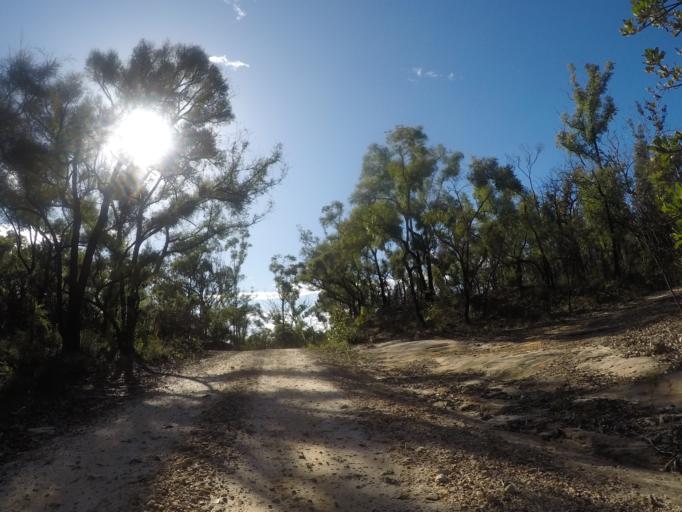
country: AU
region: New South Wales
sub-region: Hornsby Shire
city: Glenorie
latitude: -33.3331
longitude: 151.0696
